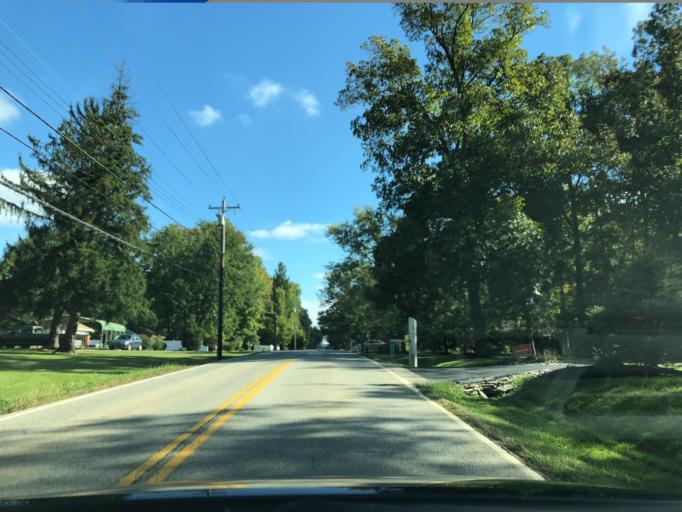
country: US
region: Ohio
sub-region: Hamilton County
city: Loveland
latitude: 39.2352
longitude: -84.2632
